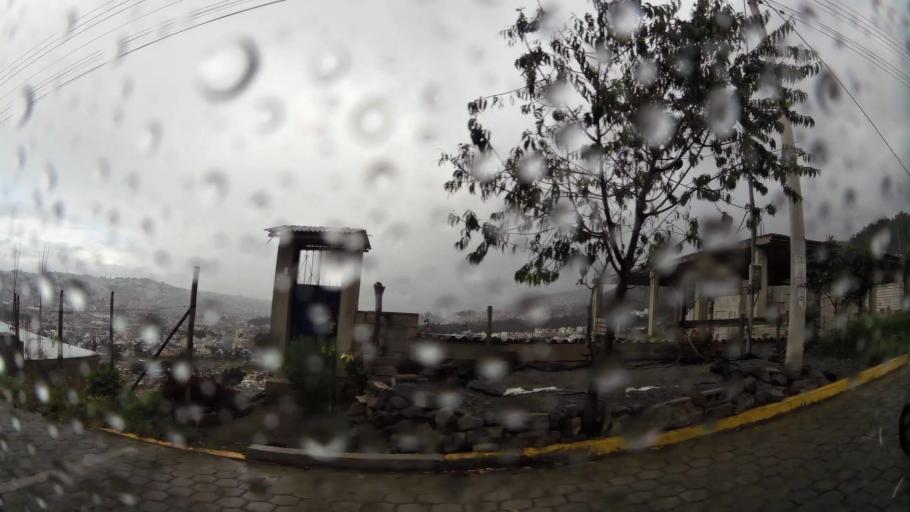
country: EC
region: Pichincha
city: Quito
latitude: -0.0987
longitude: -78.5124
